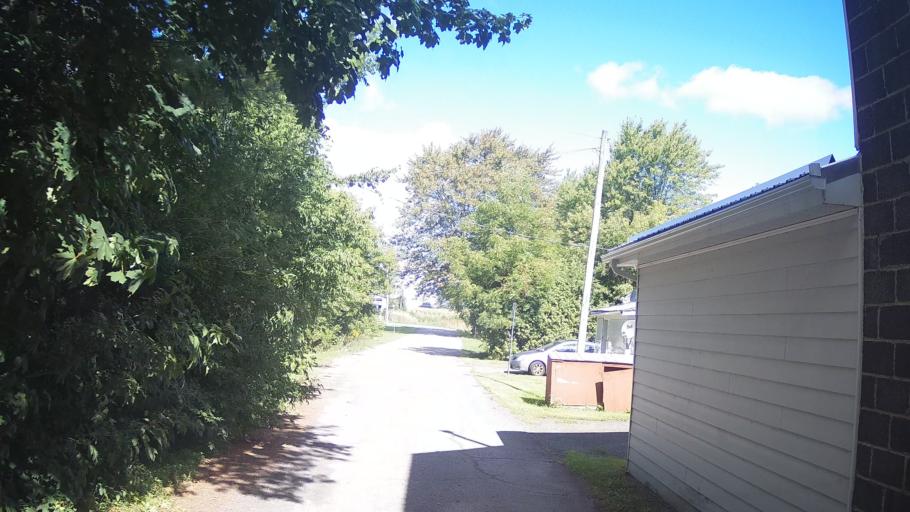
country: US
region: New York
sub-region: St. Lawrence County
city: Norfolk
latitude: 44.9756
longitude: -75.2429
